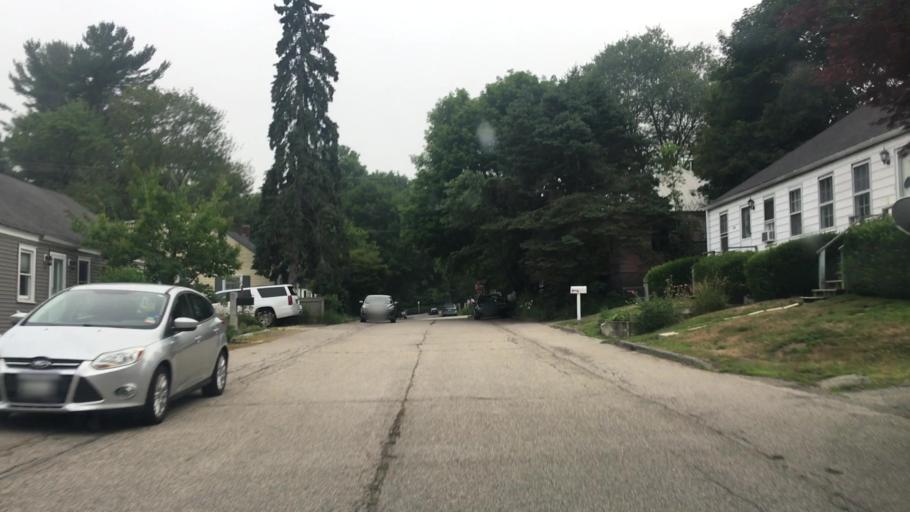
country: US
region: Maine
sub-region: York County
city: Kittery
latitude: 43.0928
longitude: -70.7323
